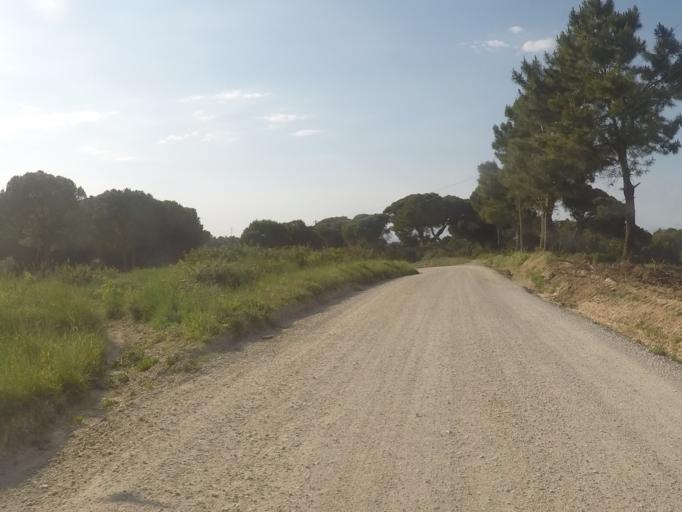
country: PT
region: Setubal
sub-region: Sesimbra
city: Sesimbra
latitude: 38.4397
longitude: -9.1916
